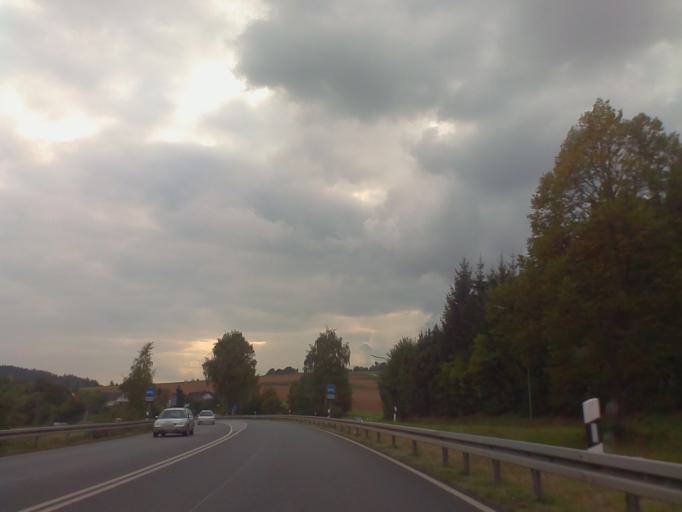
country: DE
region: Hesse
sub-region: Regierungsbezirk Kassel
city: Hunfeld
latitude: 50.6424
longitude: 9.7438
